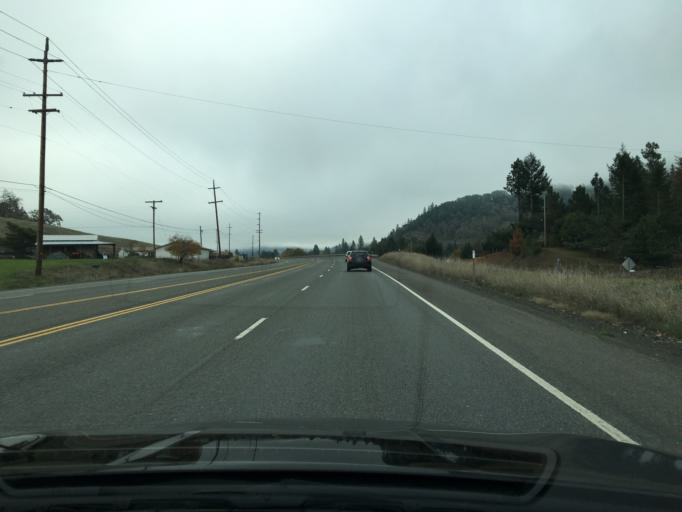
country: US
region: Oregon
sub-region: Douglas County
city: Roseburg North
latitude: 43.2110
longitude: -123.2600
